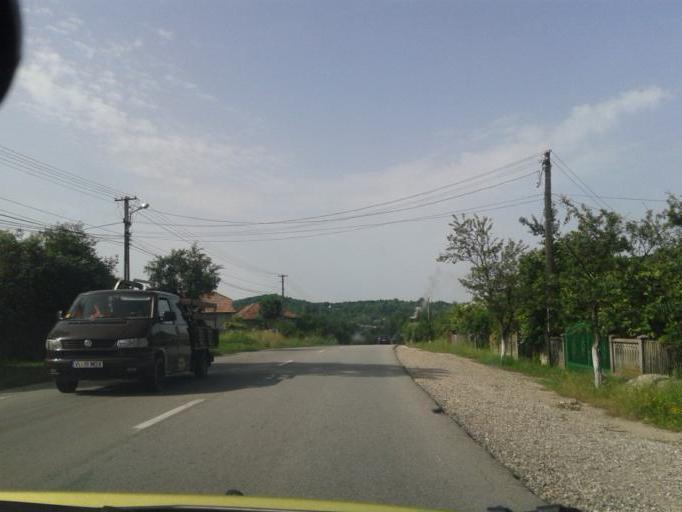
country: RO
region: Valcea
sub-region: Comuna Pietrari
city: Pietrarii de Sus
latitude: 45.1159
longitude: 24.1161
